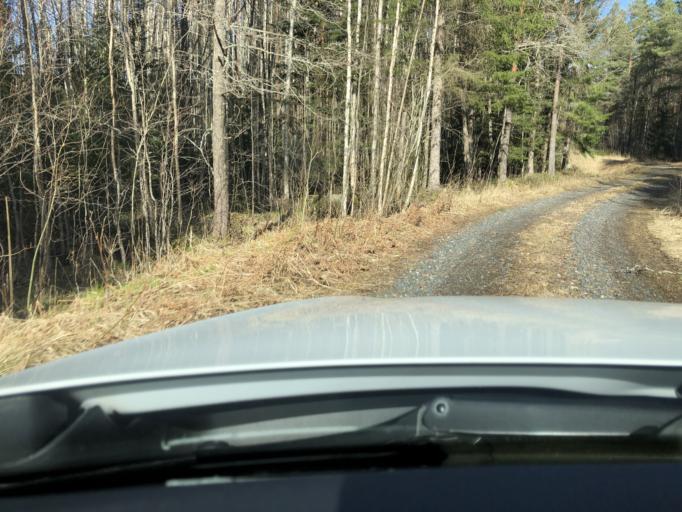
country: SE
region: Uppsala
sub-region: Heby Kommun
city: OEstervala
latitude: 60.3323
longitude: 17.1723
